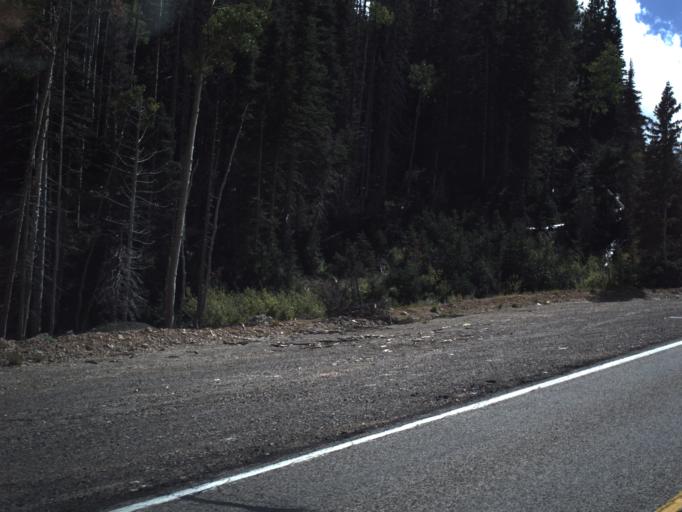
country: US
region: Utah
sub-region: Iron County
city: Cedar City
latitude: 37.5875
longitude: -112.8830
